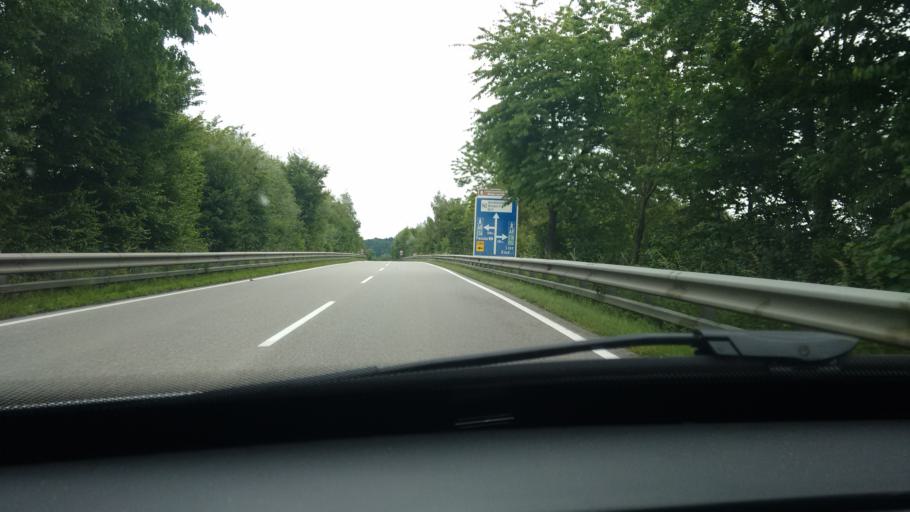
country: AT
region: Upper Austria
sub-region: Politischer Bezirk Scharding
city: Sankt Marienkirchen bei Schaerding
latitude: 48.3176
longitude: 13.4068
